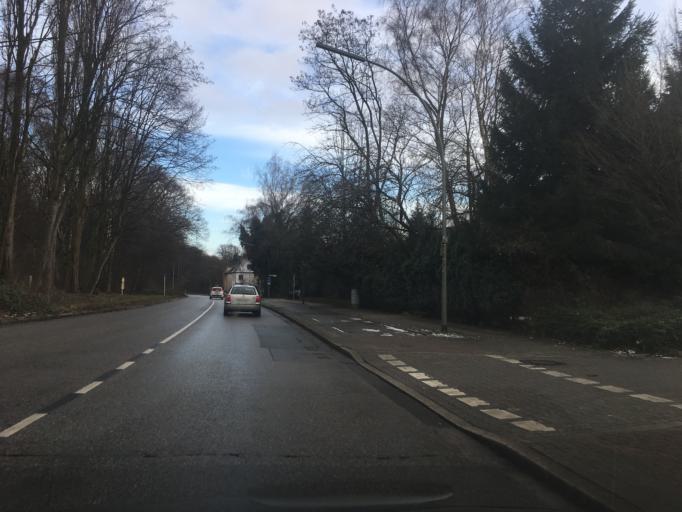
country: DE
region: North Rhine-Westphalia
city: Herten
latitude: 51.5800
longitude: 7.0688
